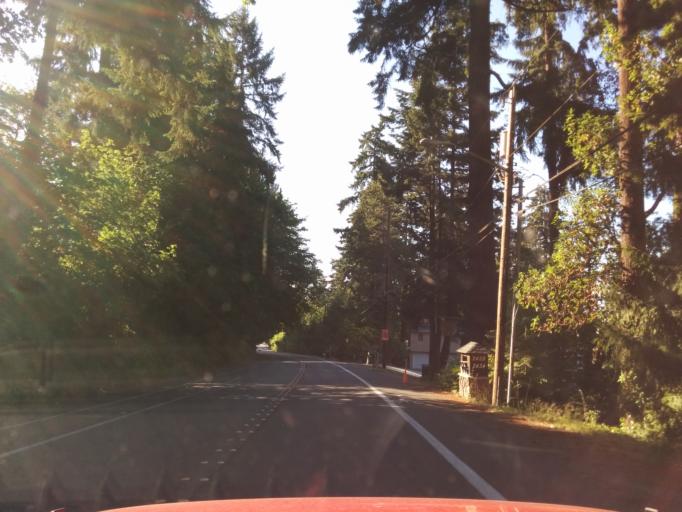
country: US
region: Washington
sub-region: King County
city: Sammamish
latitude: 47.6318
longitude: -122.0889
